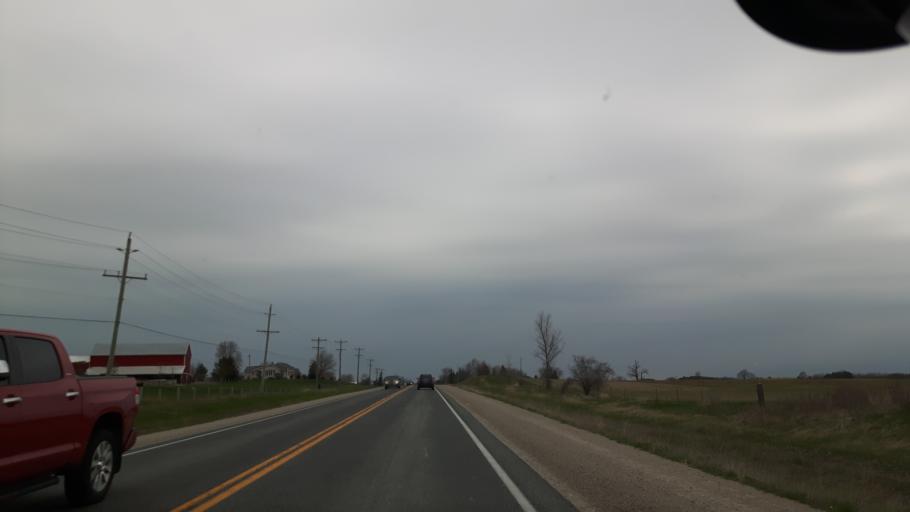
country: CA
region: Ontario
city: Goderich
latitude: 43.6761
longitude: -81.6258
